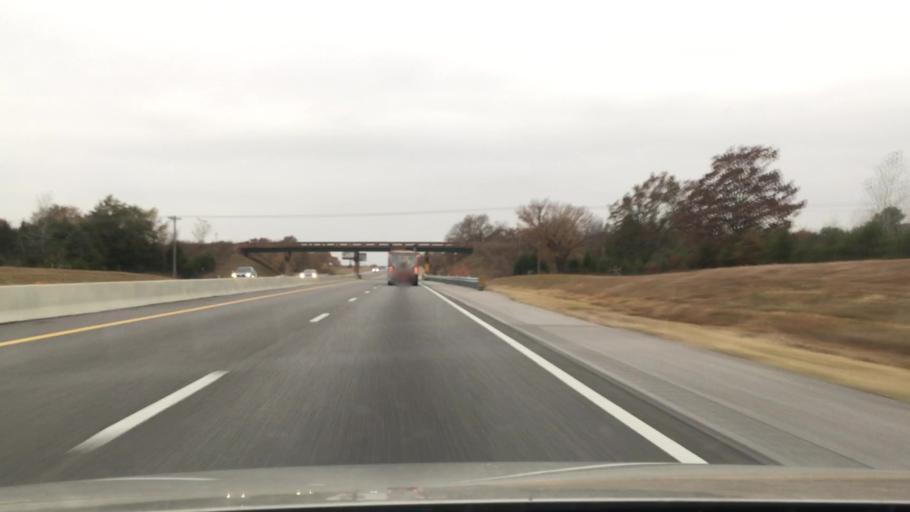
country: US
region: Oklahoma
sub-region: Lincoln County
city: Chandler
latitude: 35.7308
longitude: -96.8212
